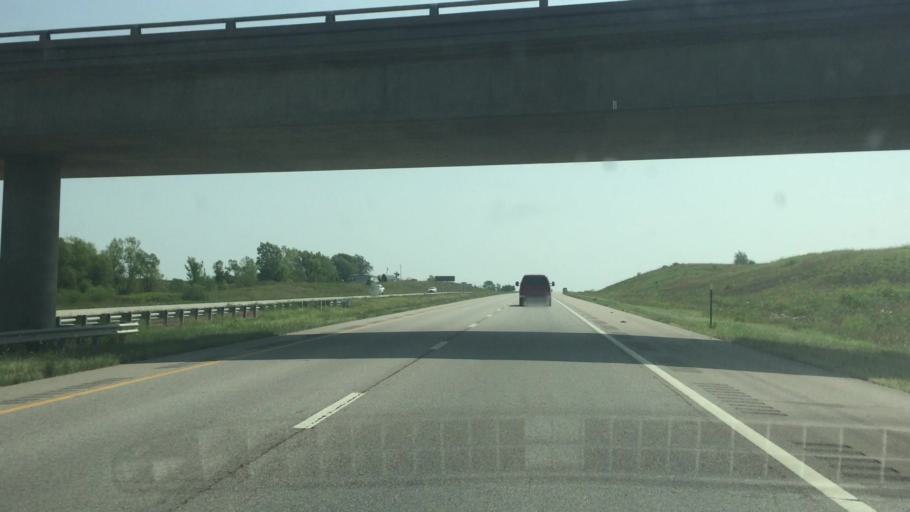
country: US
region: Kansas
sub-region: Lyon County
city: Emporia
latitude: 38.4107
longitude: -96.0796
